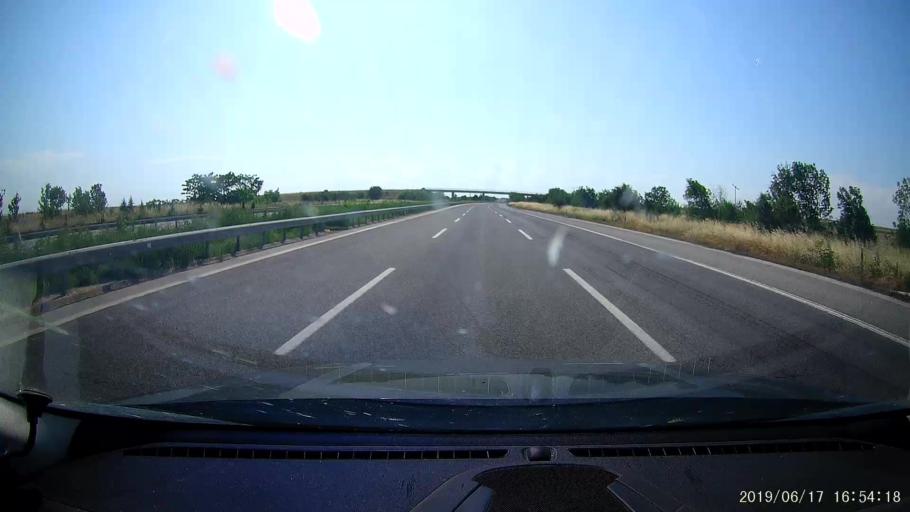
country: TR
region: Kirklareli
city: Inece
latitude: 41.5728
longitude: 27.0003
